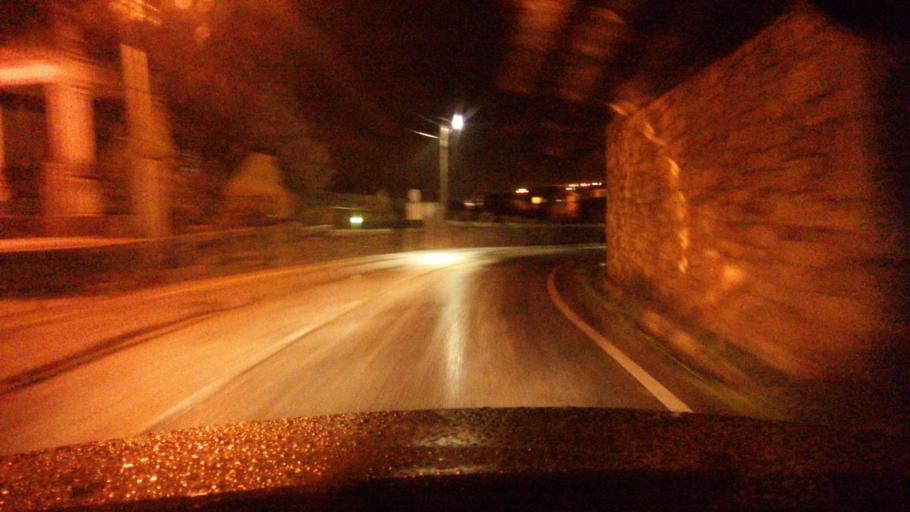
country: PT
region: Viseu
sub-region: Armamar
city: Armamar
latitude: 41.0944
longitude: -7.6860
